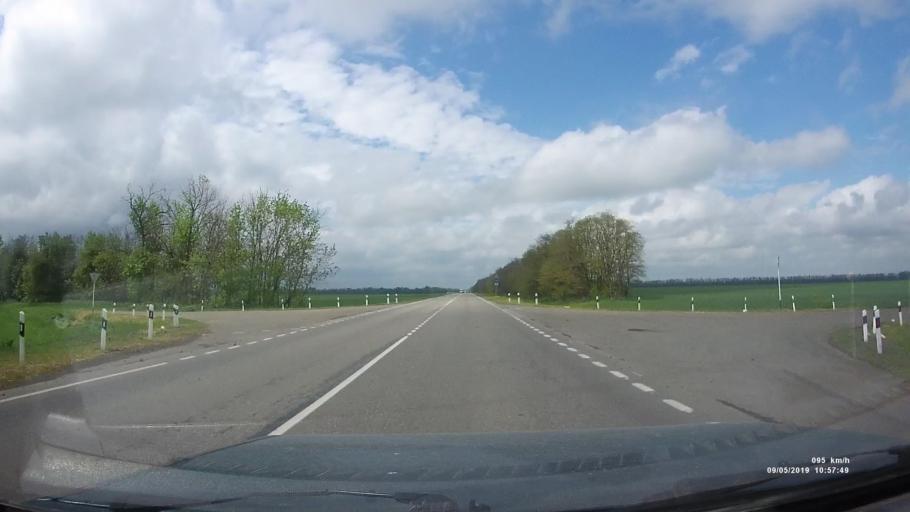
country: RU
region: Rostov
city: Peshkovo
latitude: 46.8638
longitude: 39.2717
